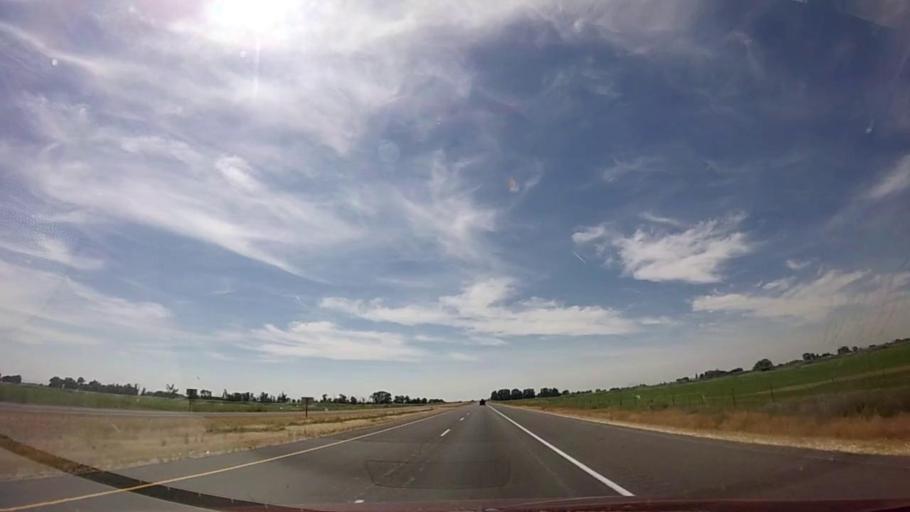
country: US
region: Idaho
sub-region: Minidoka County
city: Rupert
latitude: 42.5690
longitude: -113.6732
